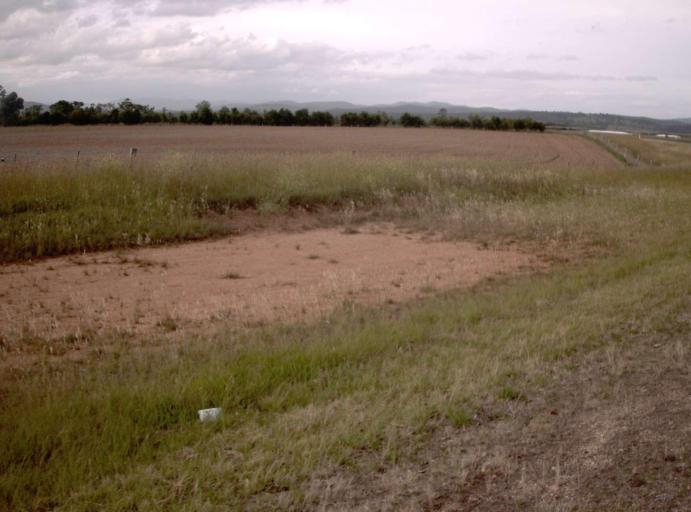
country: AU
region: Victoria
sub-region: Wellington
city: Sale
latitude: -37.8515
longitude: 147.0532
